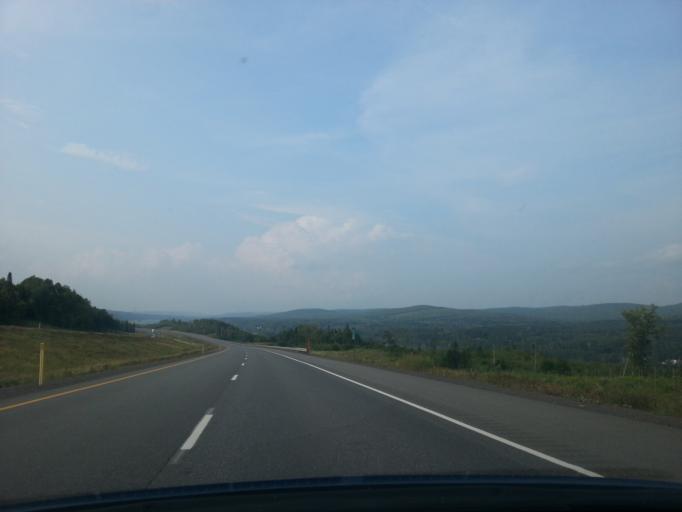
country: US
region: Maine
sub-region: Aroostook County
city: Fort Fairfield
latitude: 46.6620
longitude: -67.7310
